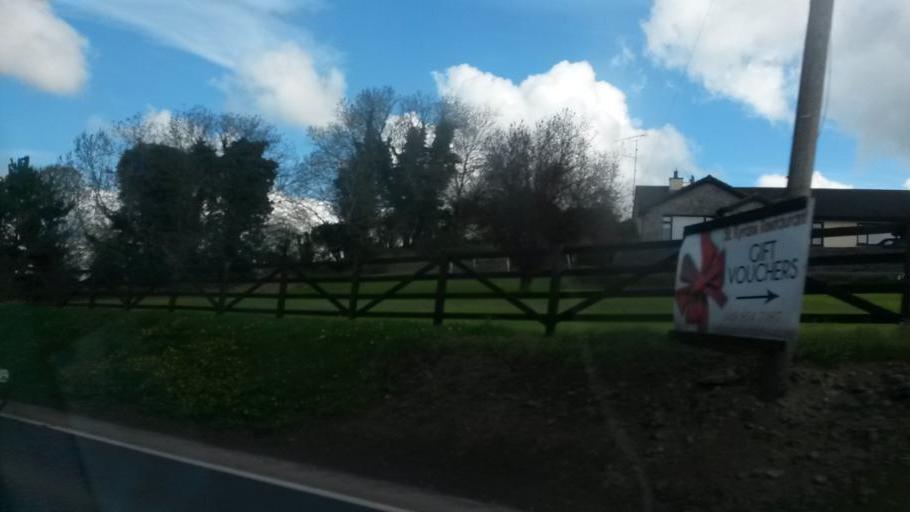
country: IE
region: Ulster
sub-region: An Cabhan
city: Virginia
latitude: 53.8254
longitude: -7.0601
